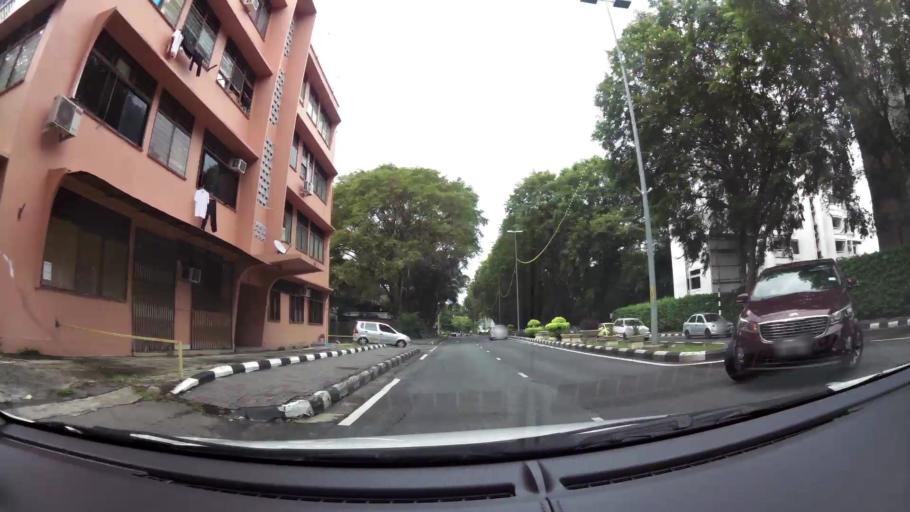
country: BN
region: Brunei and Muara
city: Bandar Seri Begawan
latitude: 4.8967
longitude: 114.9408
